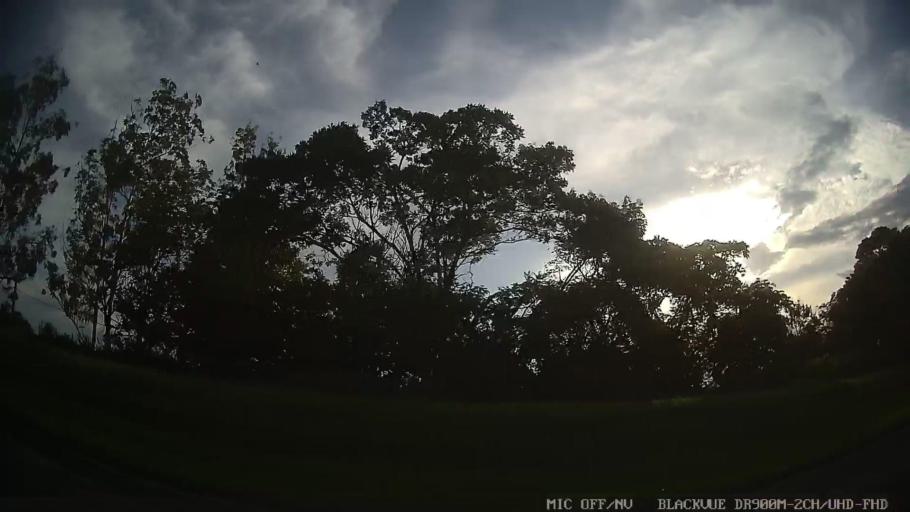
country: BR
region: Sao Paulo
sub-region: Tiete
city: Tiete
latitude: -23.1544
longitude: -47.6599
